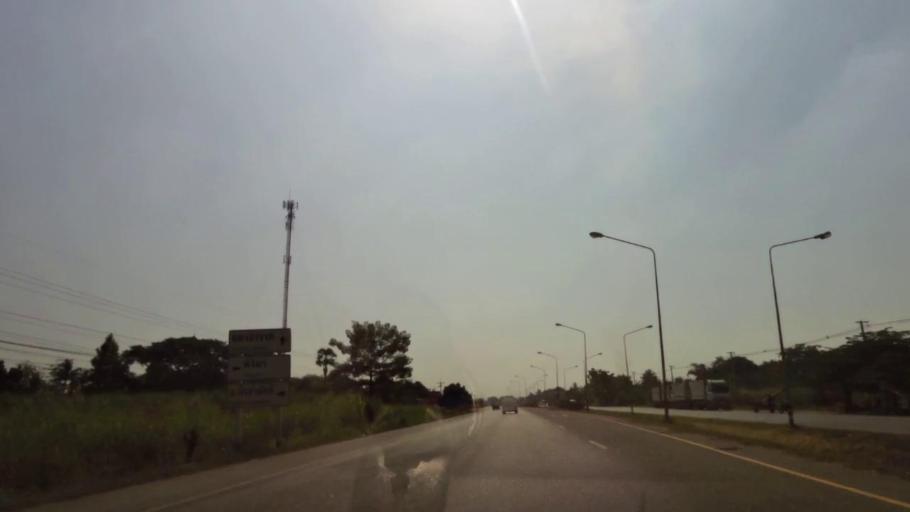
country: TH
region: Phichit
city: Wachira Barami
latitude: 16.3587
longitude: 100.1297
